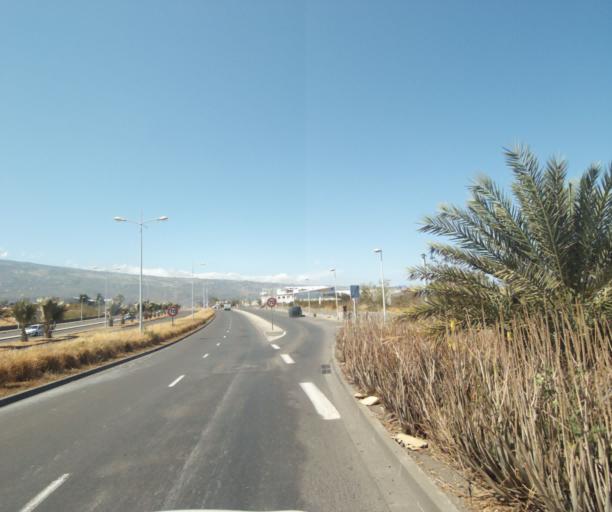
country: RE
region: Reunion
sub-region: Reunion
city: Le Port
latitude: -20.9601
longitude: 55.2936
